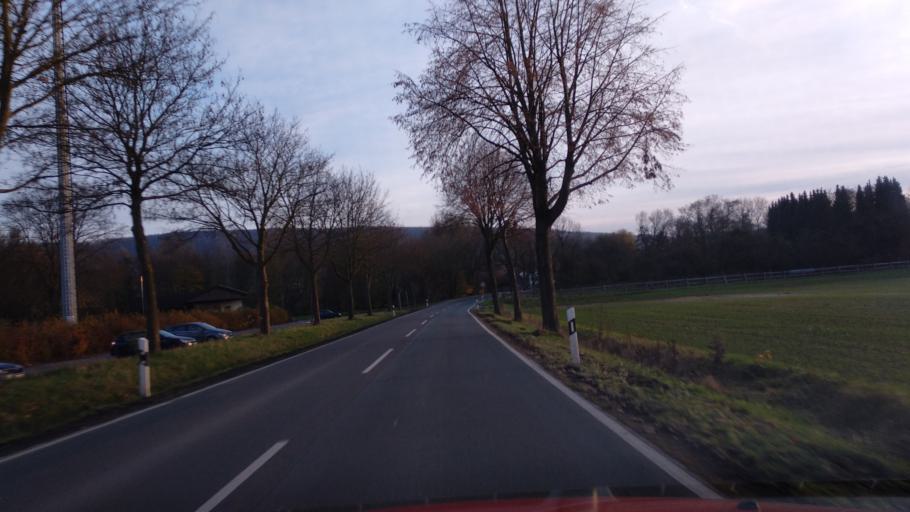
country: DE
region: Lower Saxony
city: Boffzen
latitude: 51.7171
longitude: 9.3421
